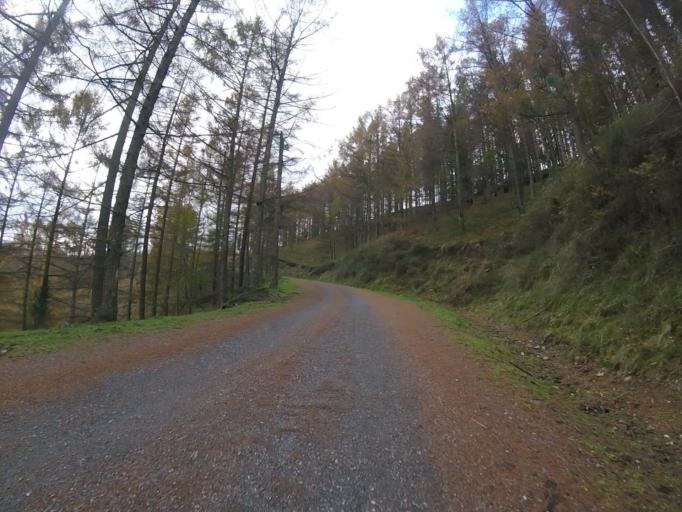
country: ES
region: Navarre
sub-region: Provincia de Navarra
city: Goizueta
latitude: 43.2120
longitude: -1.8245
